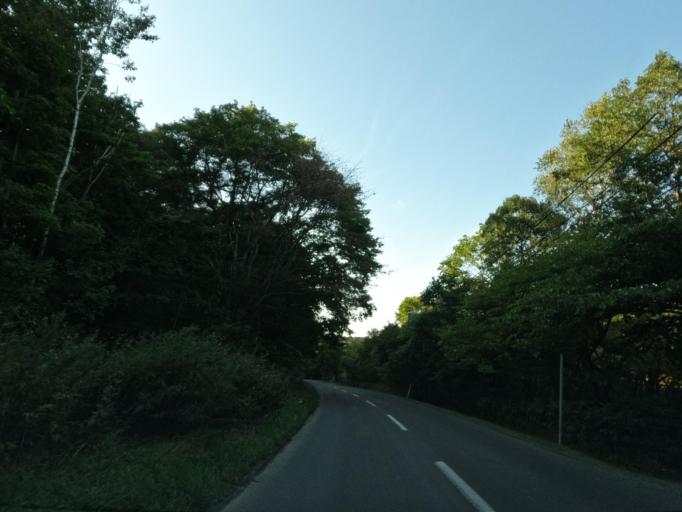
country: JP
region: Hokkaido
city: Date
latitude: 42.3988
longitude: 140.9320
